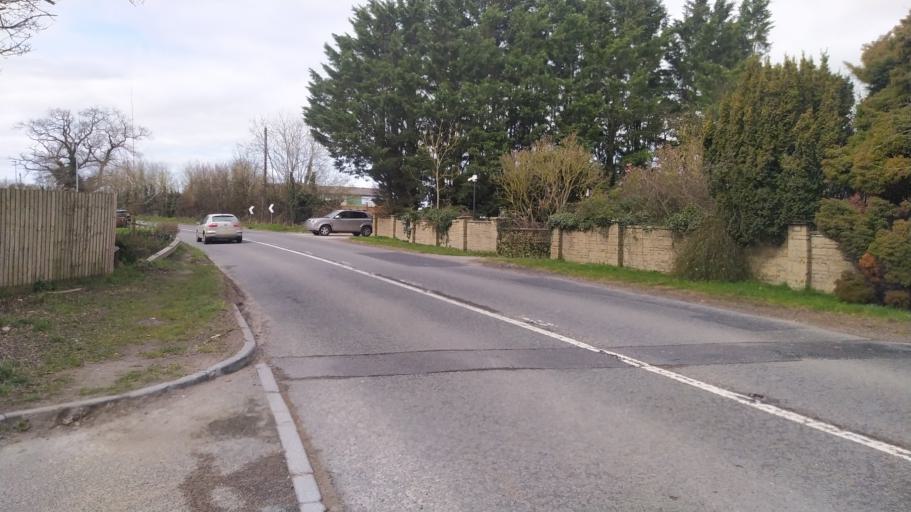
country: GB
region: England
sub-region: Wiltshire
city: Melksham
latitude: 51.3803
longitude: -2.1048
